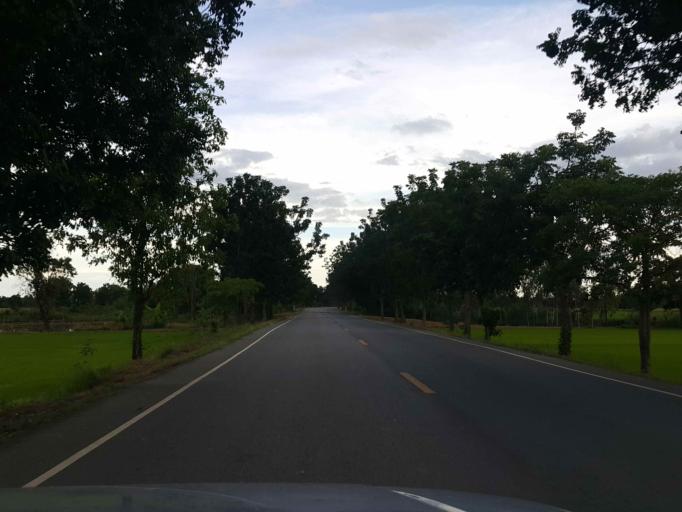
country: TH
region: Sukhothai
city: Sawankhalok
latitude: 17.3444
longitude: 99.7428
